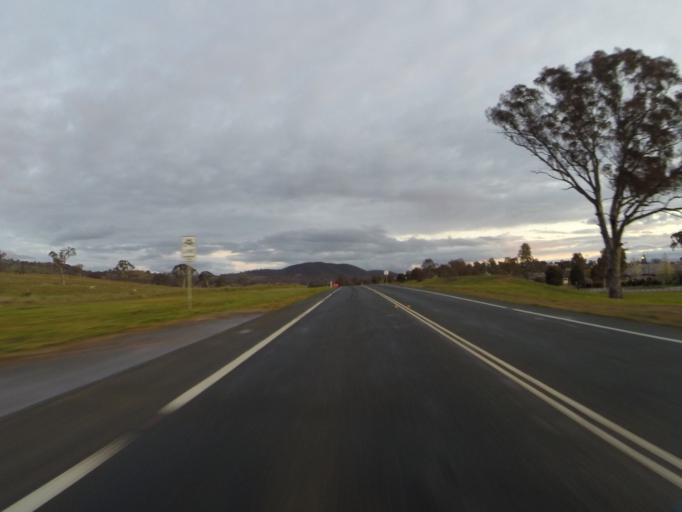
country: AU
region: Australian Capital Territory
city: Kaleen
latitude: -35.1955
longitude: 149.1620
